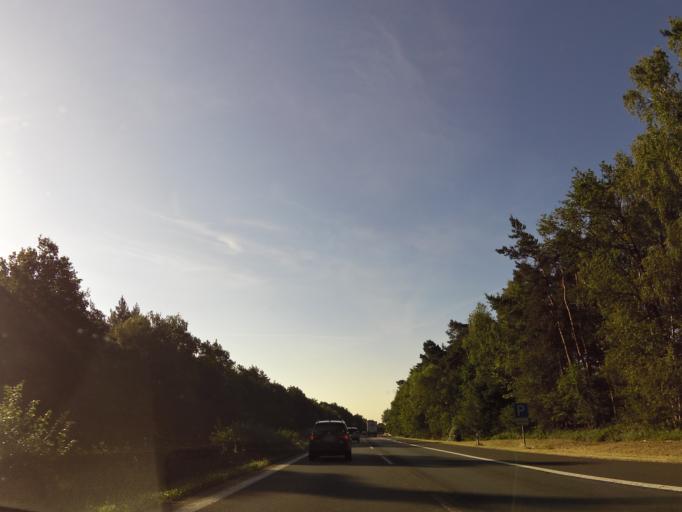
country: DE
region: Bavaria
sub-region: Regierungsbezirk Mittelfranken
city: Grossenseebach
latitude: 49.6631
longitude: 10.8887
